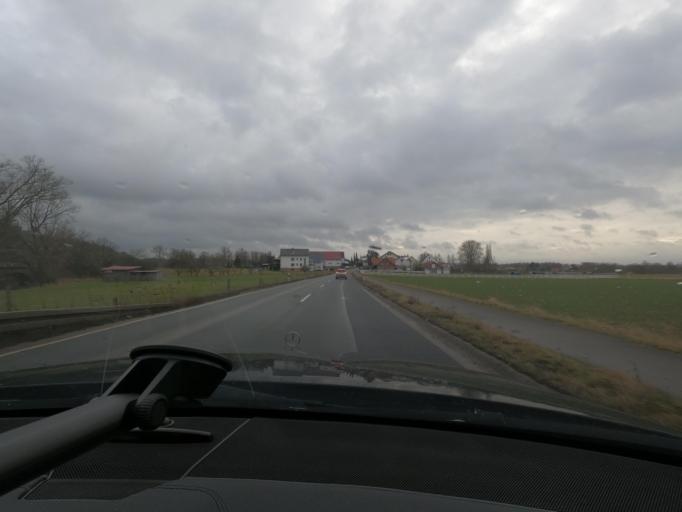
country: DE
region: Hesse
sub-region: Regierungsbezirk Kassel
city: Volkmarsen
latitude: 51.4201
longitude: 9.1234
